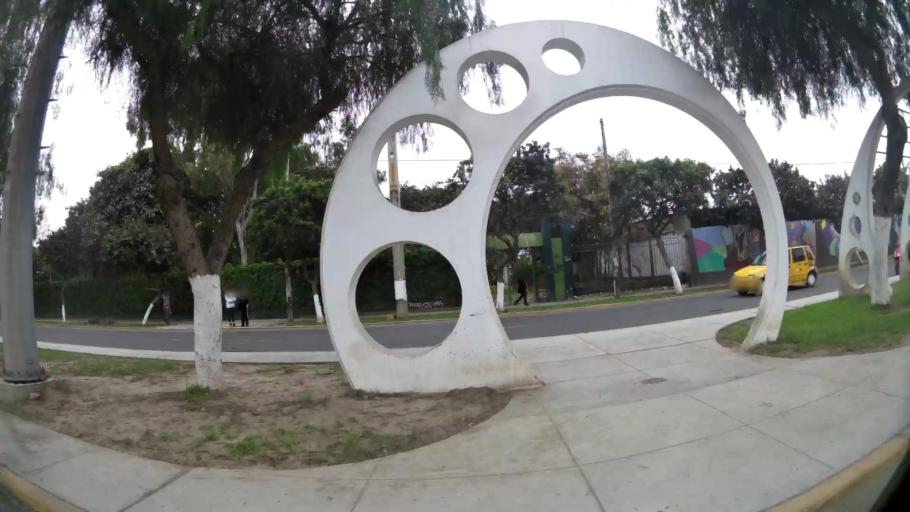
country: PE
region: La Libertad
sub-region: Provincia de Trujillo
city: Trujillo
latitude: -8.1255
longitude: -79.0364
